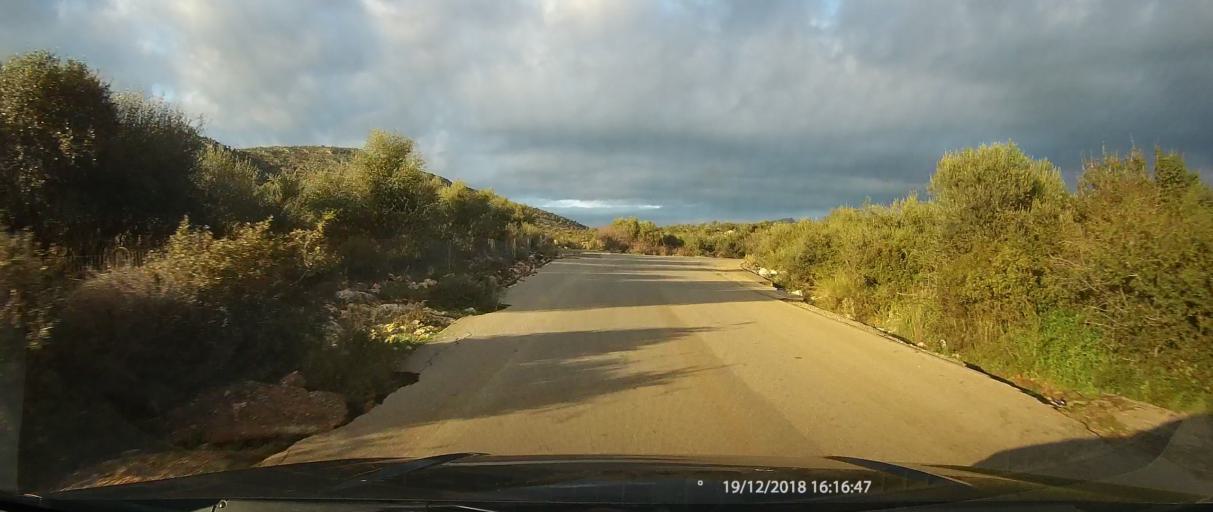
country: GR
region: Peloponnese
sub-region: Nomos Lakonias
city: Kato Glikovrisi
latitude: 36.9040
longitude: 22.8060
